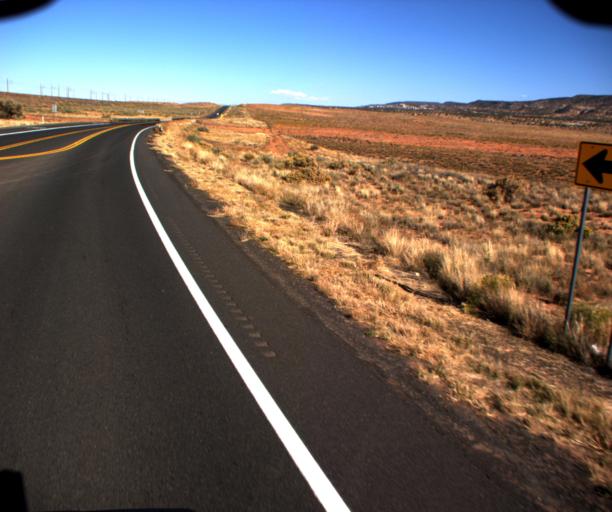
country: US
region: Arizona
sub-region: Coconino County
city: Kaibito
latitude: 36.3915
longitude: -110.8795
